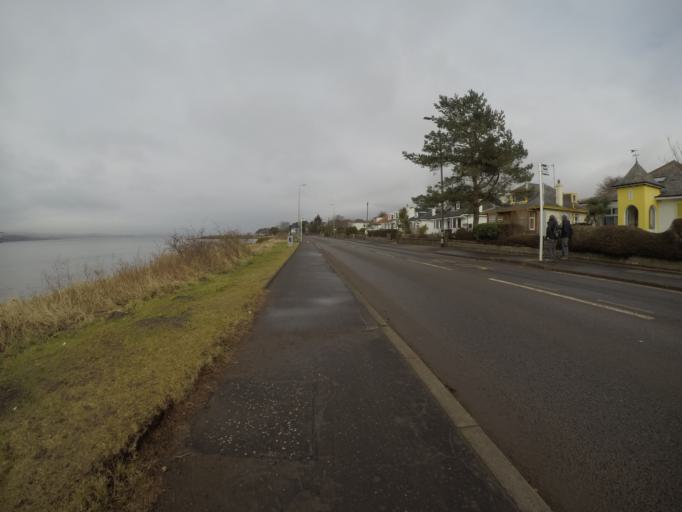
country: GB
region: Scotland
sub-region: North Ayrshire
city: Fairlie
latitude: 55.7487
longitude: -4.8569
